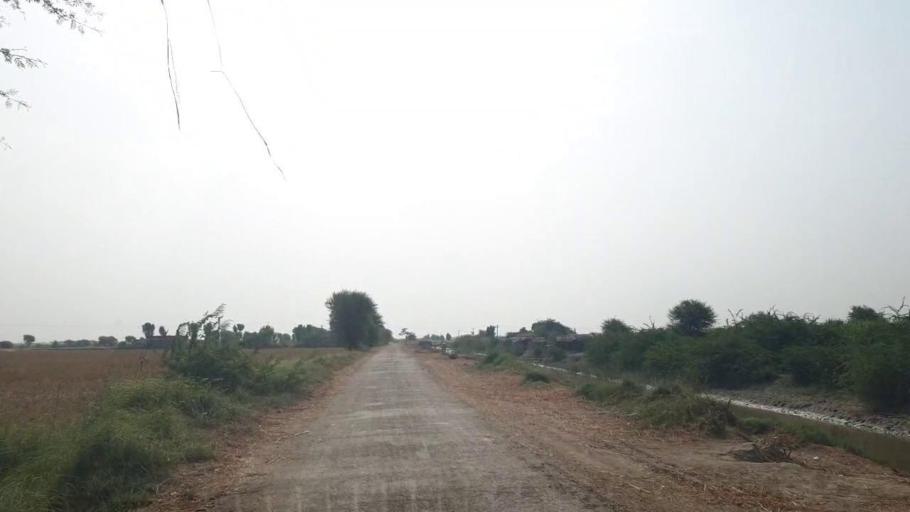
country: PK
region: Sindh
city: Badin
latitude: 24.7569
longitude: 68.7608
